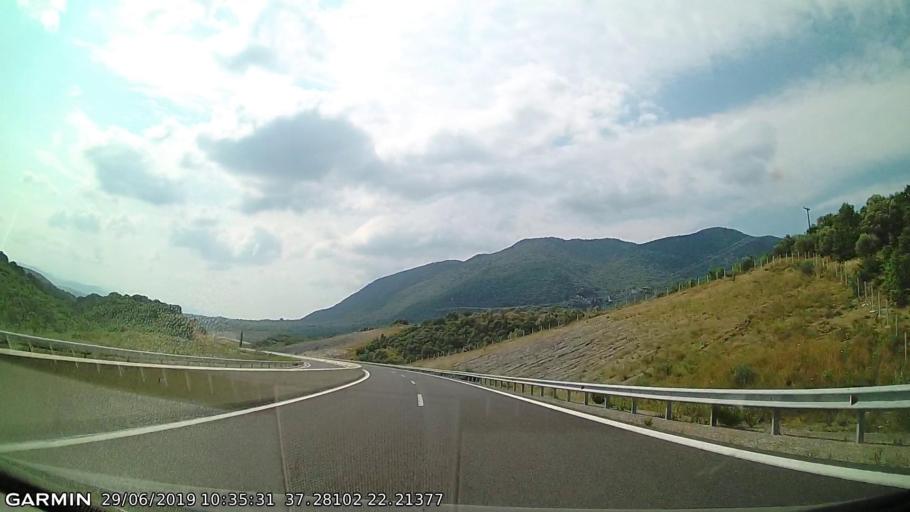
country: GR
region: Peloponnese
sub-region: Nomos Arkadias
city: Megalopoli
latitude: 37.2808
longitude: 22.2138
